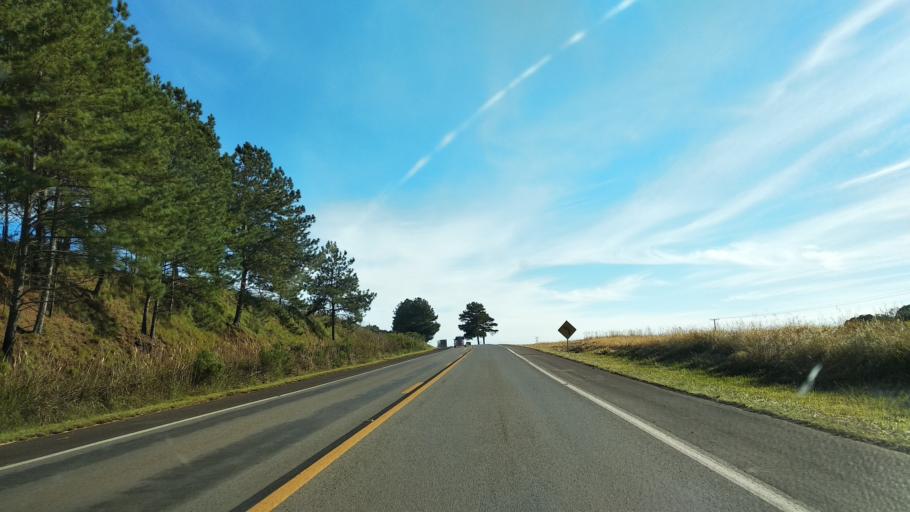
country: BR
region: Santa Catarina
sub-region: Celso Ramos
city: Celso Ramos
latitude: -27.5322
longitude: -51.3960
